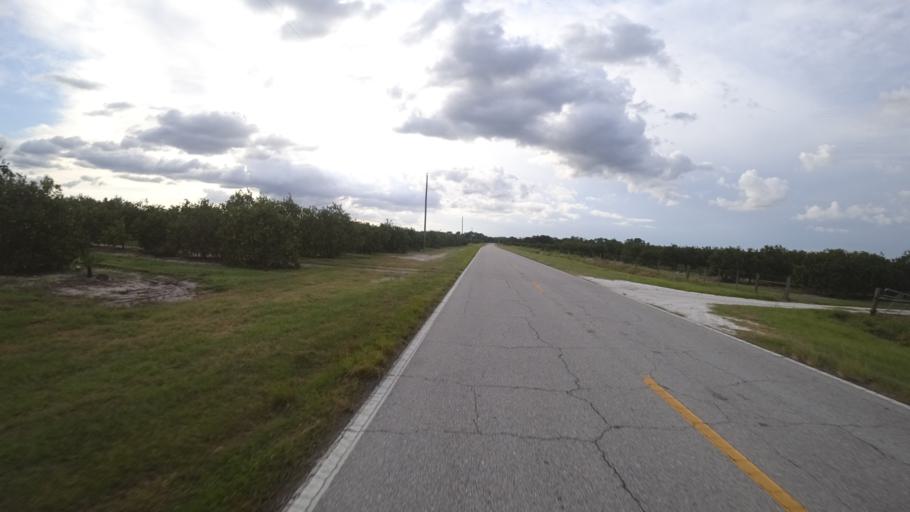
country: US
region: Florida
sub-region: Hillsborough County
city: Wimauma
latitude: 27.5373
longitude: -82.0959
